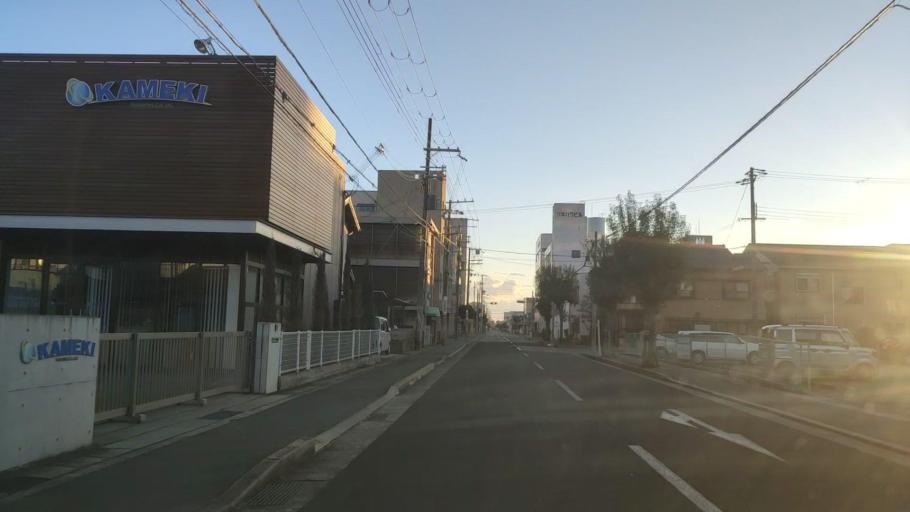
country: JP
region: Hyogo
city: Himeji
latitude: 34.8237
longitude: 134.6846
